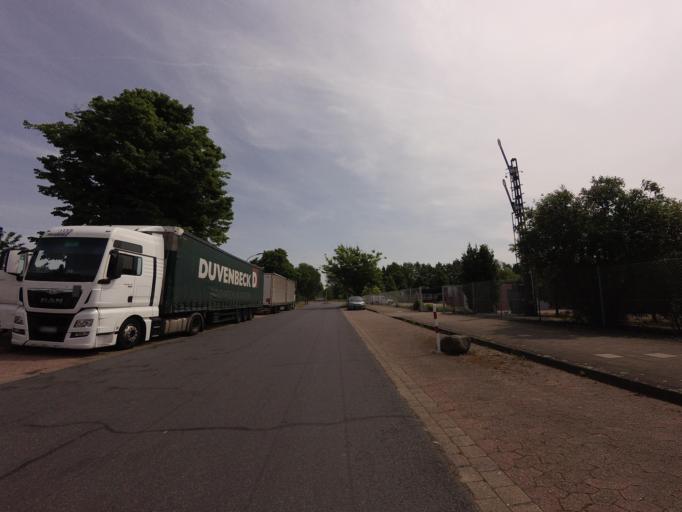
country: DE
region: Lower Saxony
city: Braunschweig
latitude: 52.3092
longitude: 10.4825
